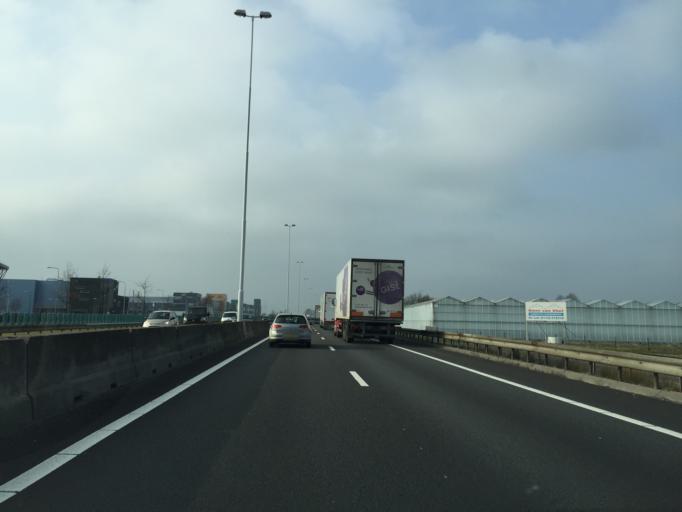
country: NL
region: South Holland
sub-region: Gemeente Westland
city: Maasdijk
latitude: 51.9595
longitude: 4.2290
